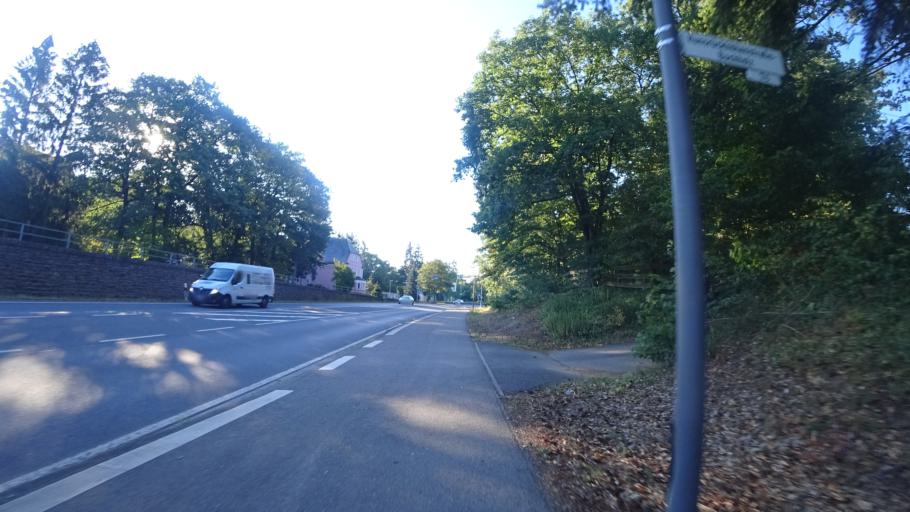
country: DE
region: Rheinland-Pfalz
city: Kratzenburg
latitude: 50.2122
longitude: 7.5501
